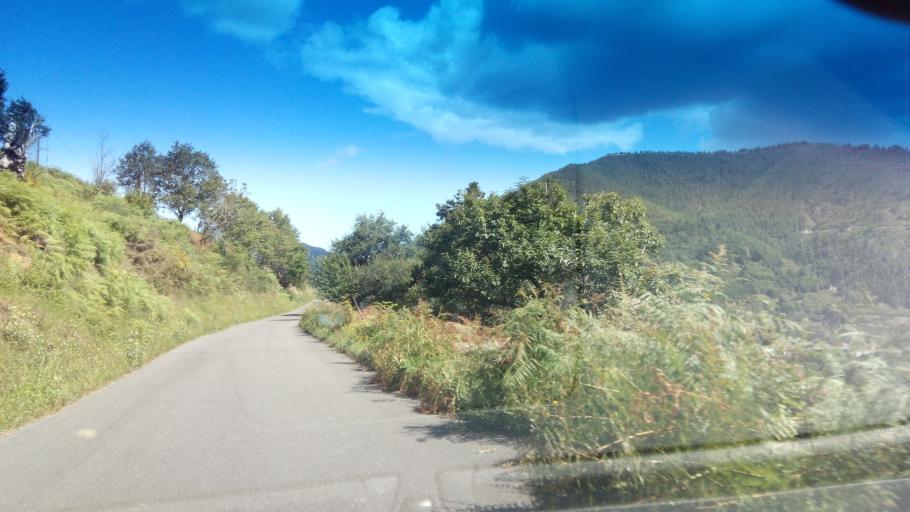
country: ES
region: Asturias
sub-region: Province of Asturias
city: Parres
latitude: 43.3732
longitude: -5.1731
